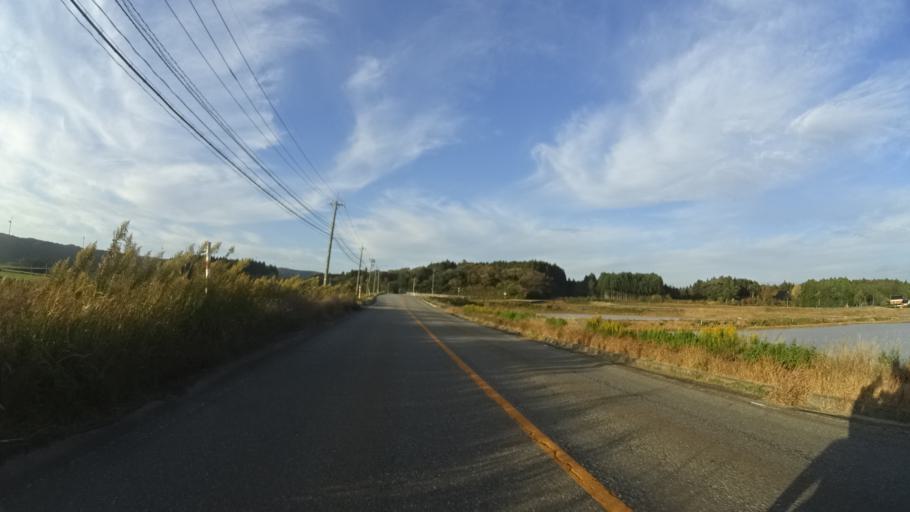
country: JP
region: Ishikawa
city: Nanao
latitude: 37.1607
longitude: 136.7166
